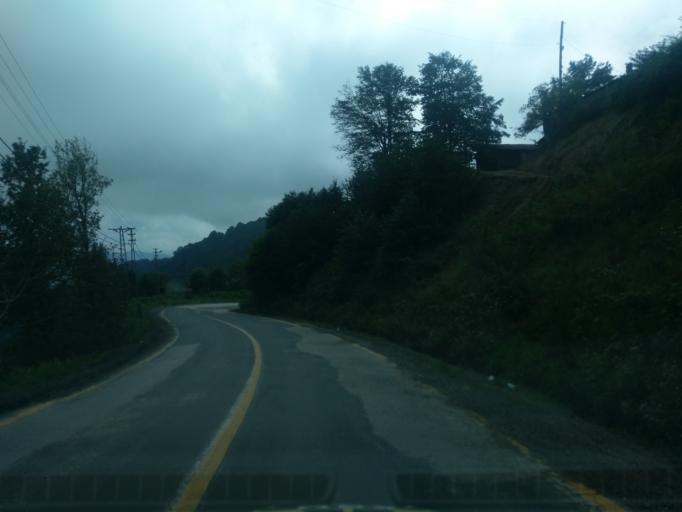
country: TR
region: Ordu
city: Gurgentepe
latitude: 40.8489
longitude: 37.6554
